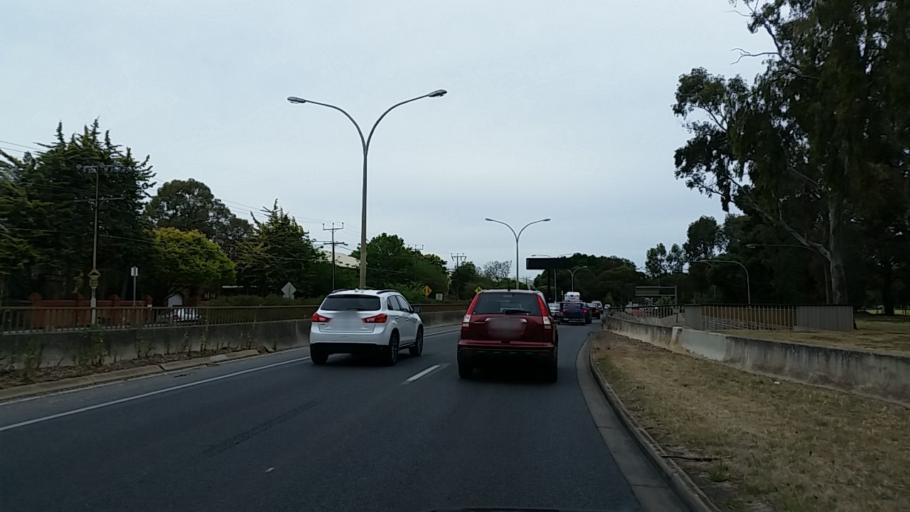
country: AU
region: South Australia
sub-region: Adelaide
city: North Adelaide
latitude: -34.9056
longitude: 138.6127
